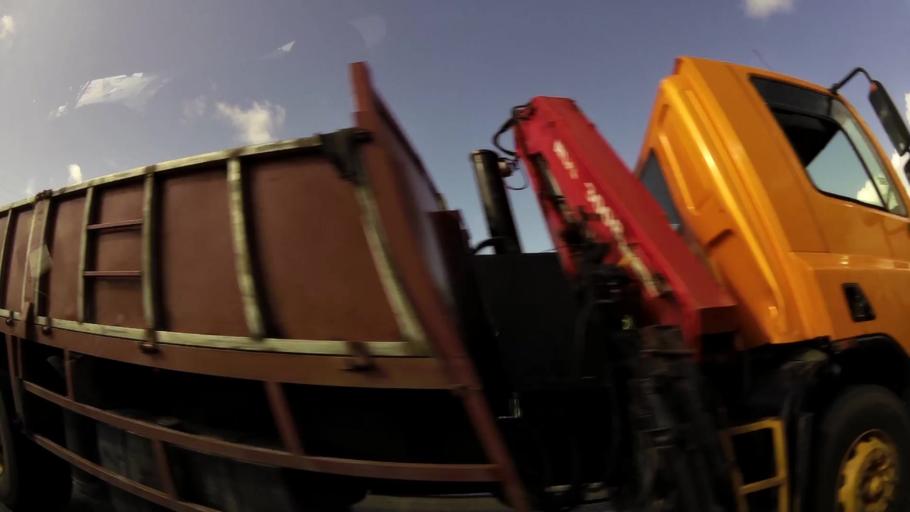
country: GY
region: Demerara-Mahaica
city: Mahaica Village
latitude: 6.7599
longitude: -57.9844
